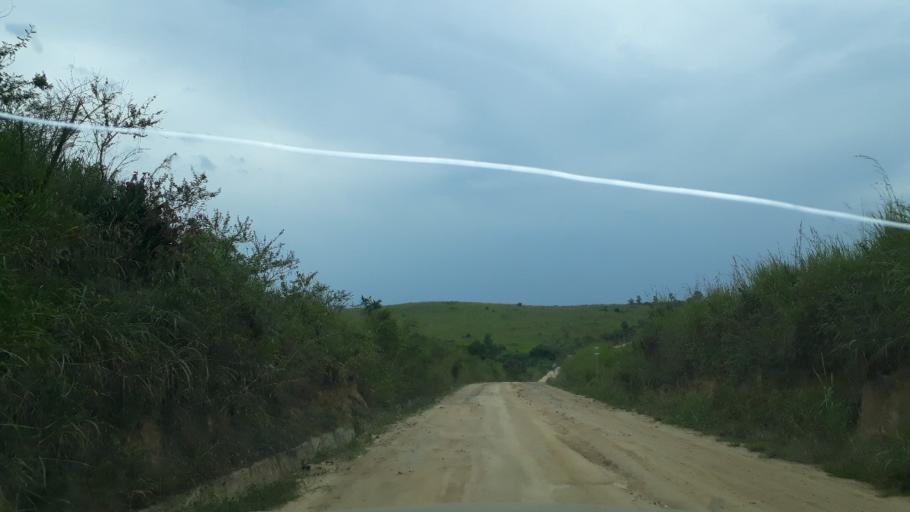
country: CD
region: Eastern Province
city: Bunia
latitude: 1.4742
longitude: 30.1132
